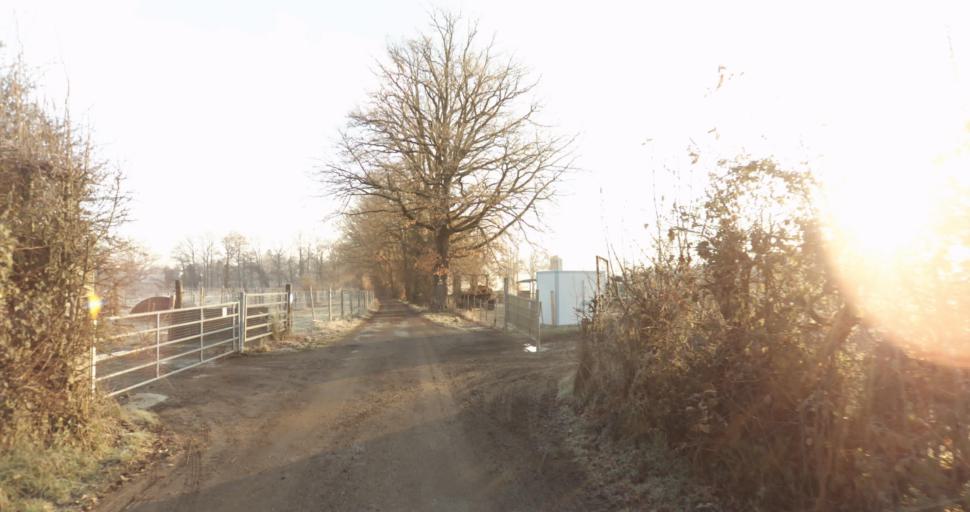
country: FR
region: Limousin
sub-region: Departement de la Haute-Vienne
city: Aixe-sur-Vienne
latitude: 45.7958
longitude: 1.1631
